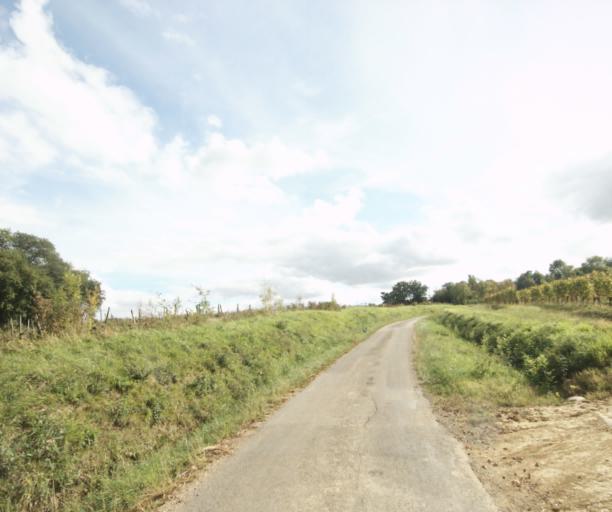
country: FR
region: Midi-Pyrenees
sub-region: Departement du Gers
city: Gondrin
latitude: 43.8505
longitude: 0.2747
